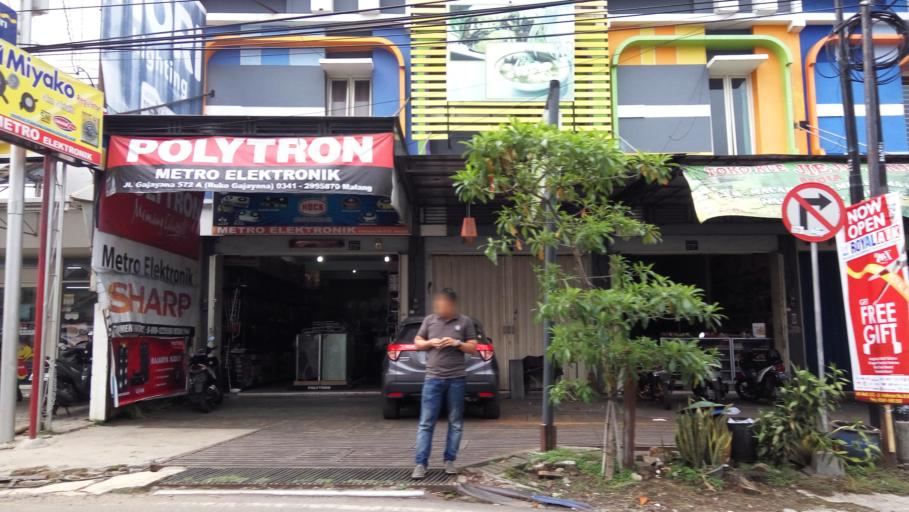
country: ID
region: East Java
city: Malang
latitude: -7.9457
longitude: 112.6094
